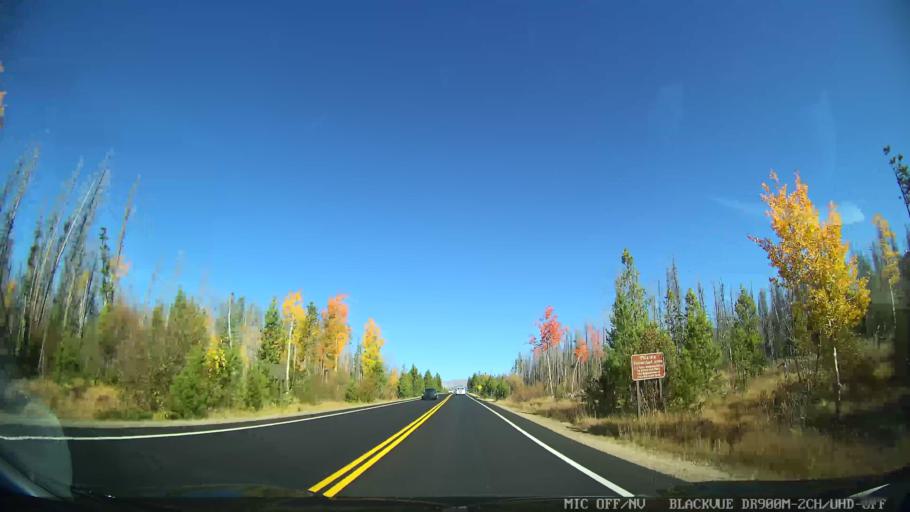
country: US
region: Colorado
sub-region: Grand County
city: Granby
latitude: 40.2624
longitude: -105.8311
